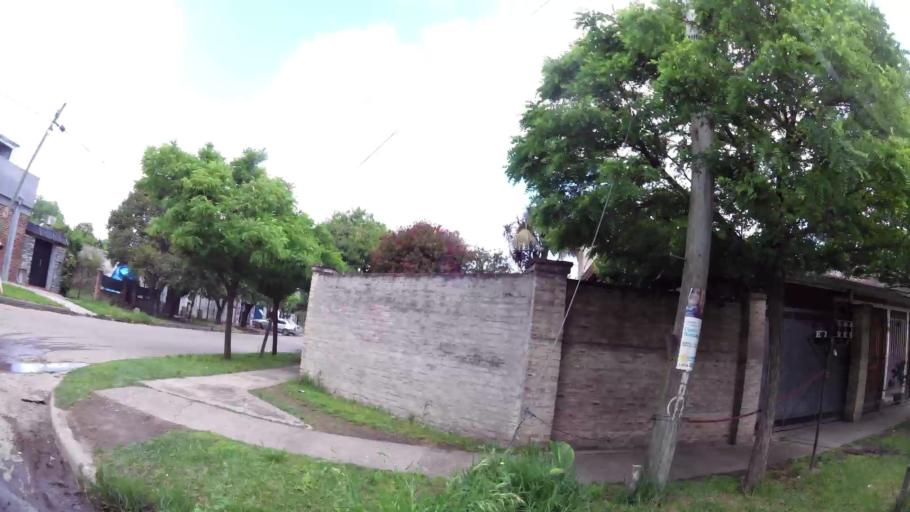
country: AR
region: Buenos Aires
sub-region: Partido de Quilmes
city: Quilmes
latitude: -34.8282
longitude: -58.2230
